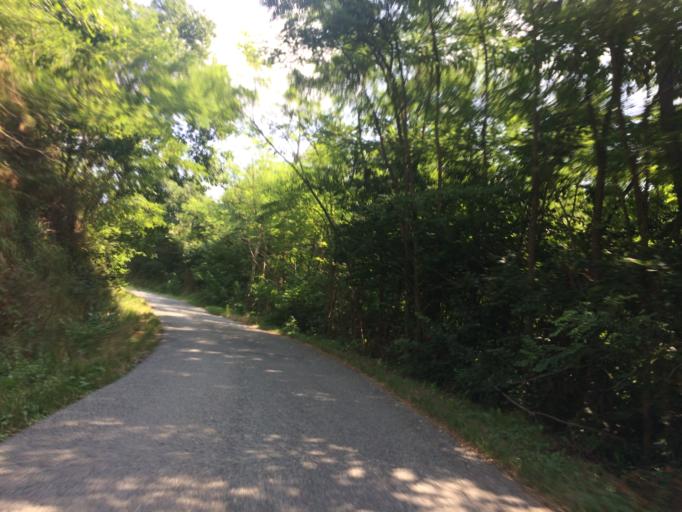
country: IT
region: Piedmont
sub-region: Provincia di Alessandria
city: Pareto
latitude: 44.4909
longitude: 8.3516
